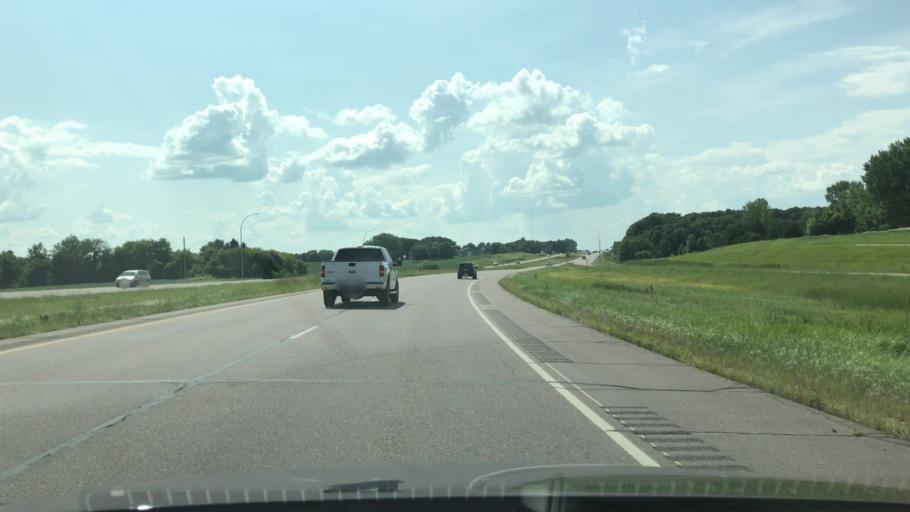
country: US
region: Minnesota
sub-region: Nicollet County
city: North Mankato
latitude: 44.1450
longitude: -94.0861
